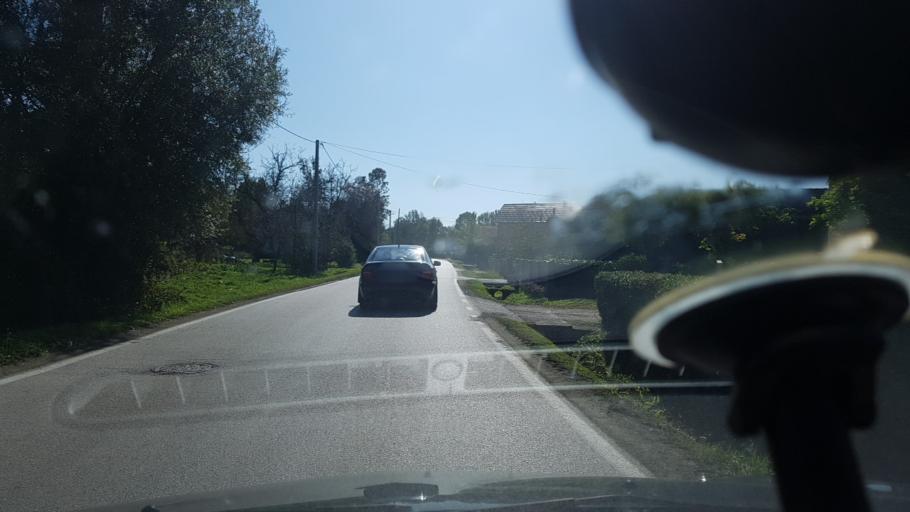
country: HR
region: Zagrebacka
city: Lupoglav
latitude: 45.7453
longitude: 16.3028
